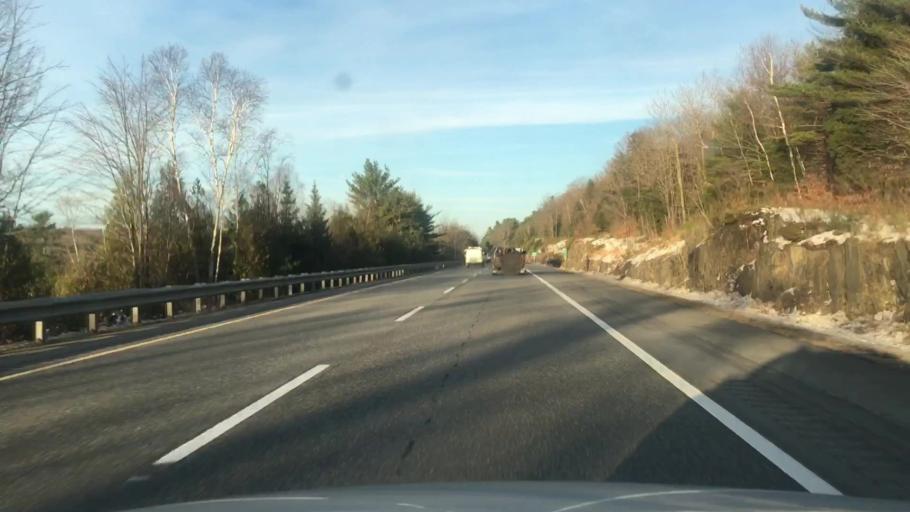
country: US
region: Maine
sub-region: Kennebec County
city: Sidney
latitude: 44.3810
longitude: -69.7667
